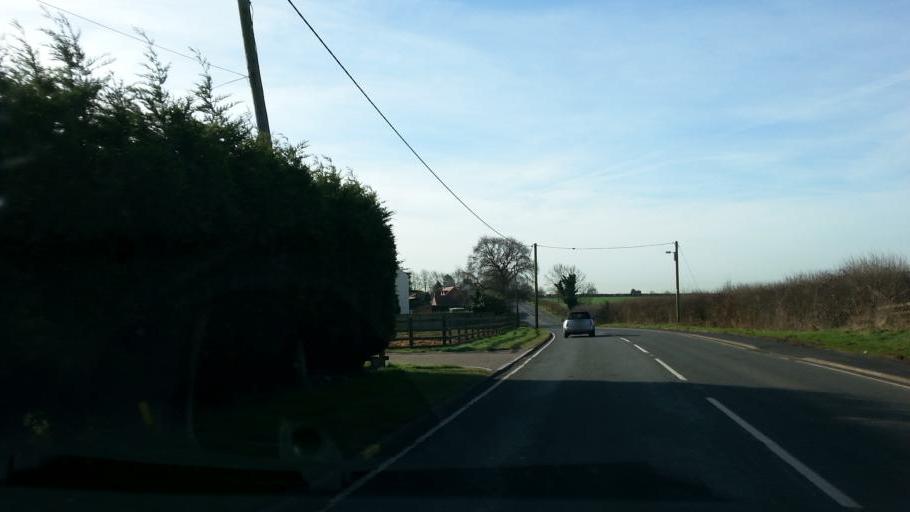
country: GB
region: England
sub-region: Leicestershire
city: Hinckley
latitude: 52.5019
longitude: -1.3652
